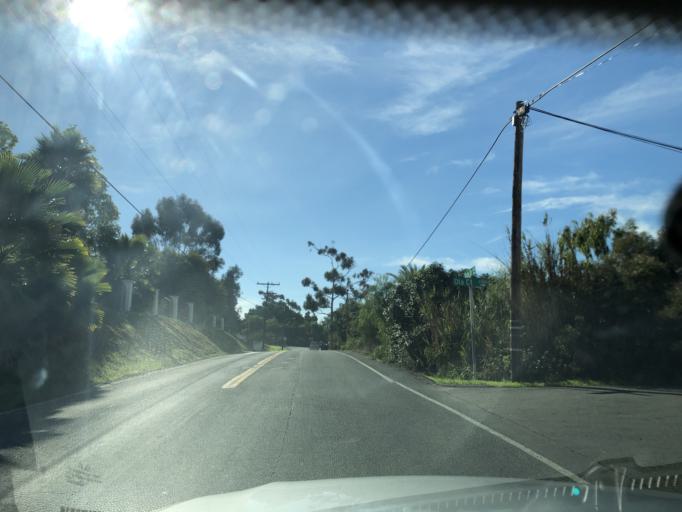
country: US
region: California
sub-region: San Diego County
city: Chula Vista
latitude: 32.6441
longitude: -117.0616
